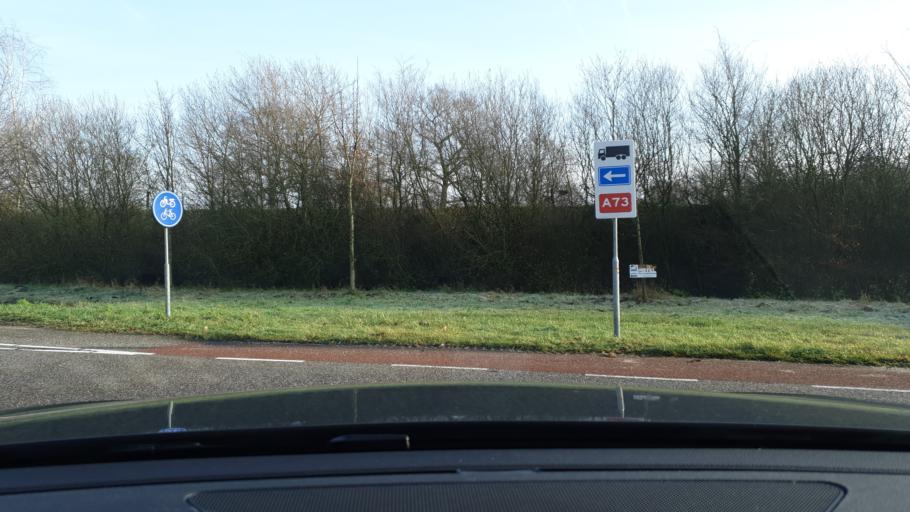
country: NL
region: Limburg
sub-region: Gemeente Peel en Maas
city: Maasbree
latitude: 51.4325
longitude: 6.0907
